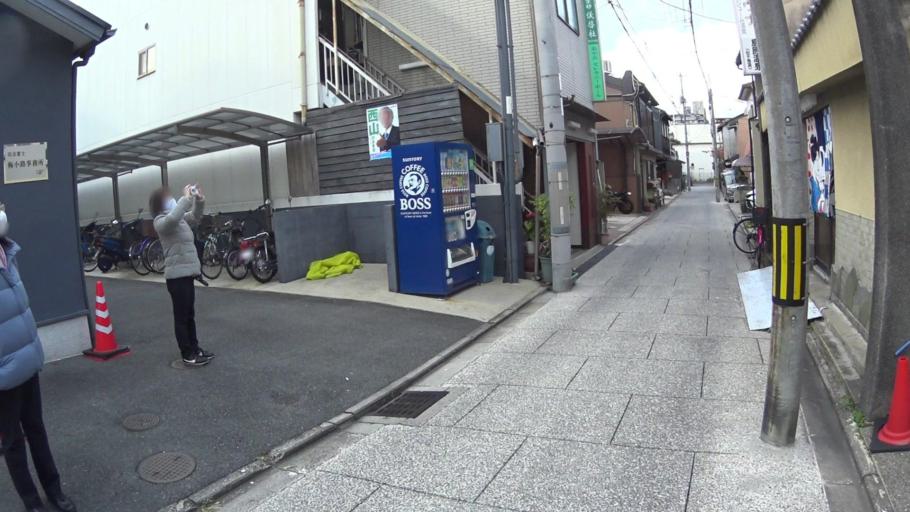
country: JP
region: Kyoto
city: Kyoto
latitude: 34.9930
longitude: 135.7441
